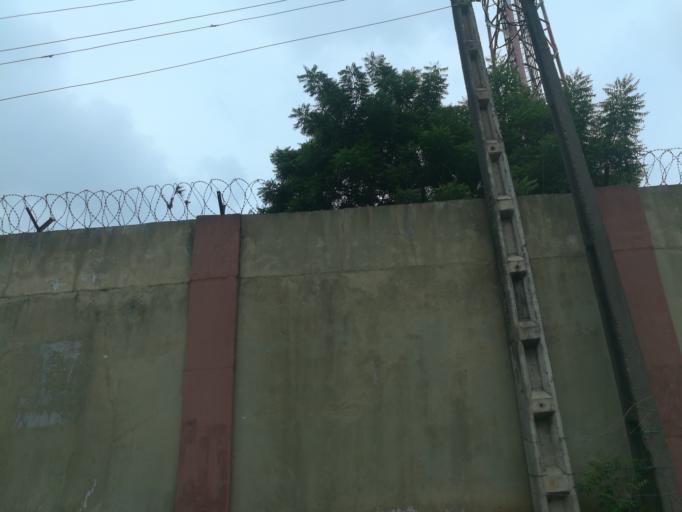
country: NG
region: Lagos
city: Ojota
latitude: 6.5636
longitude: 3.3654
